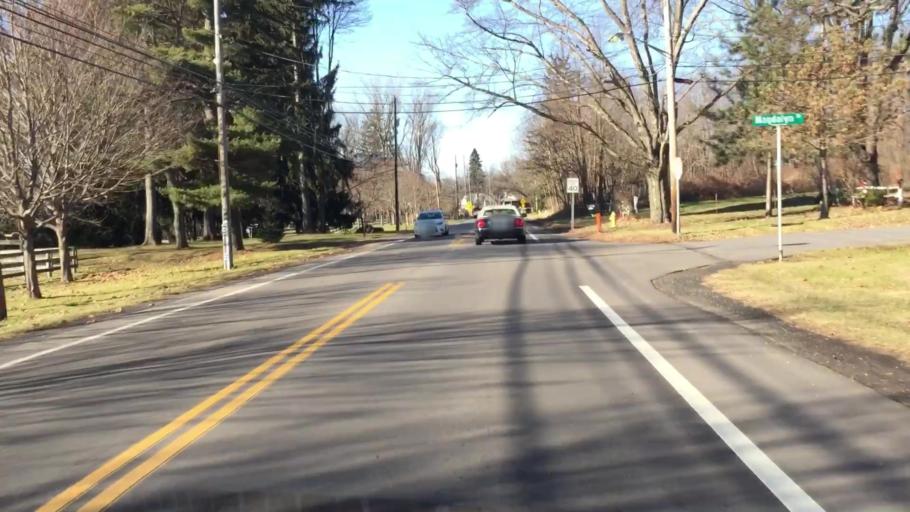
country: US
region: Ohio
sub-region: Summit County
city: Fairlawn
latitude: 41.0869
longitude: -81.6009
